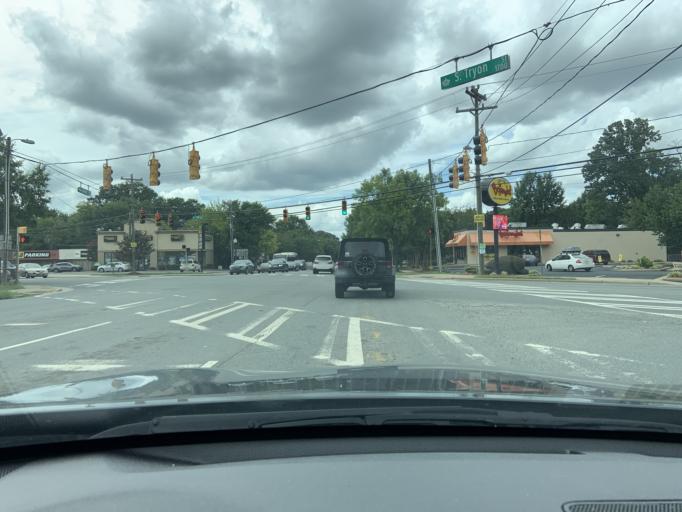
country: US
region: North Carolina
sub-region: Mecklenburg County
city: Charlotte
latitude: 35.2139
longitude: -80.8615
